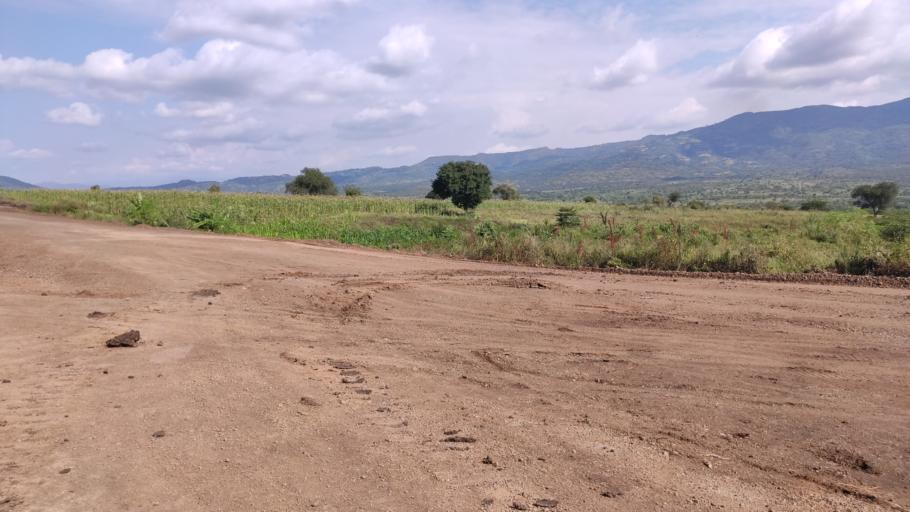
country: ET
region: Southern Nations, Nationalities, and People's Region
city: Felege Neway
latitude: 6.3976
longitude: 37.1128
